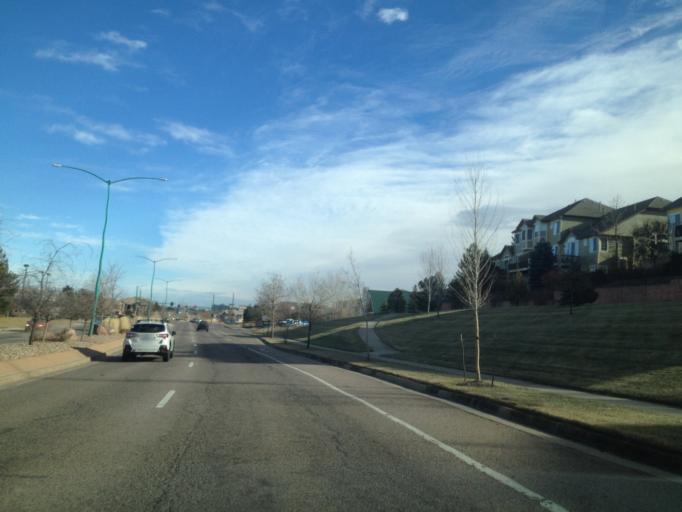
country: US
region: Colorado
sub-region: Boulder County
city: Superior
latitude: 39.9288
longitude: -105.1504
